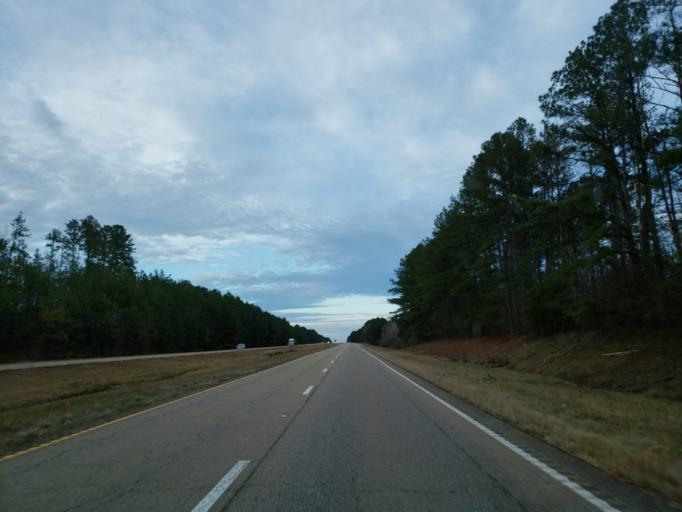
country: US
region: Mississippi
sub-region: Lauderdale County
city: Meridian Station
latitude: 32.5614
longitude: -88.5044
